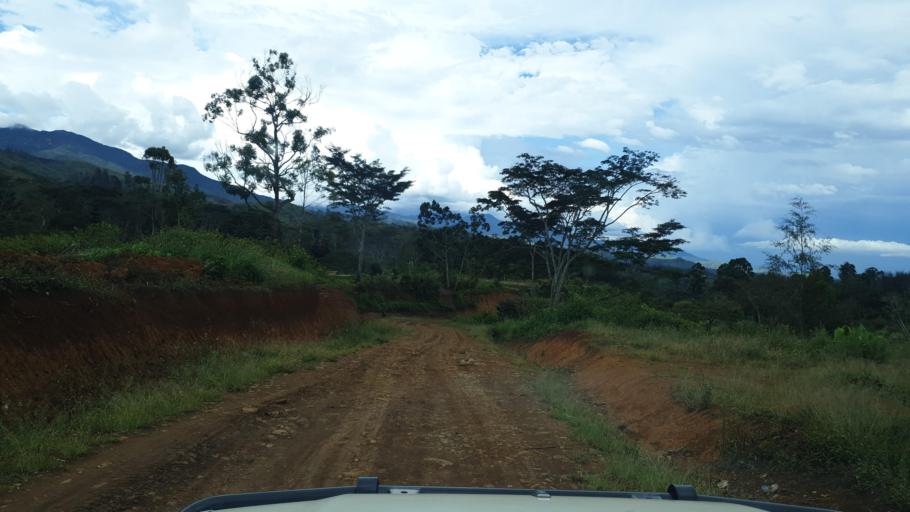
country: PG
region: Eastern Highlands
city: Goroka
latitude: -5.9626
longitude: 145.2681
